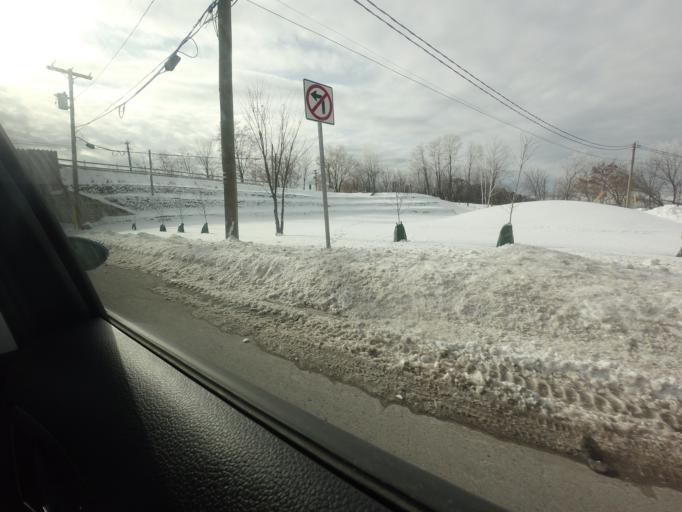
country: CA
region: New Brunswick
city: Fredericton
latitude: 45.9583
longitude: -66.6239
